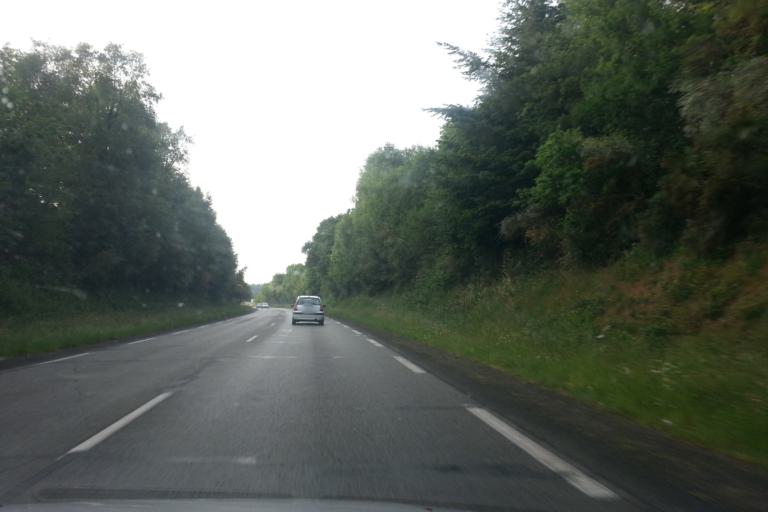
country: FR
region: Brittany
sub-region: Departement du Morbihan
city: Caudan
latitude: 47.8094
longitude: -3.3348
